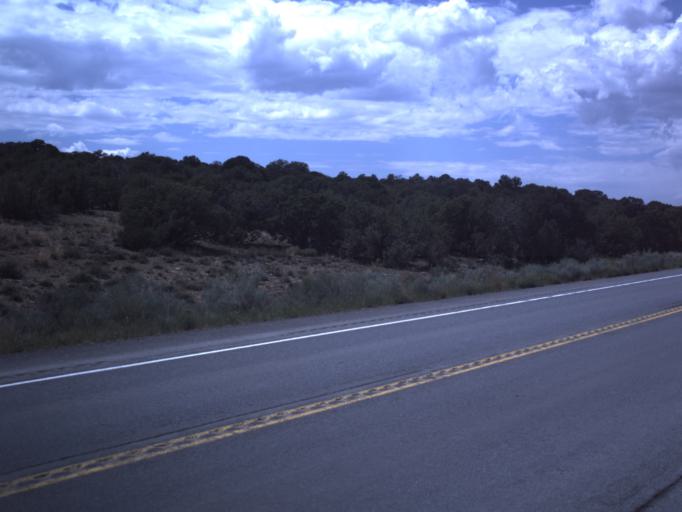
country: US
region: Utah
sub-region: Duchesne County
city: Duchesne
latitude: 40.1769
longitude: -110.5090
